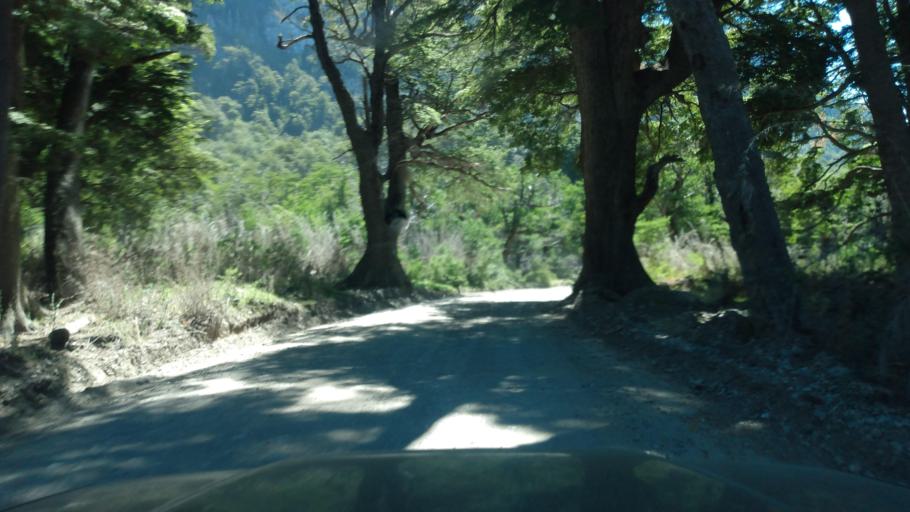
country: AR
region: Neuquen
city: Villa La Angostura
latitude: -40.6200
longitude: -71.6029
